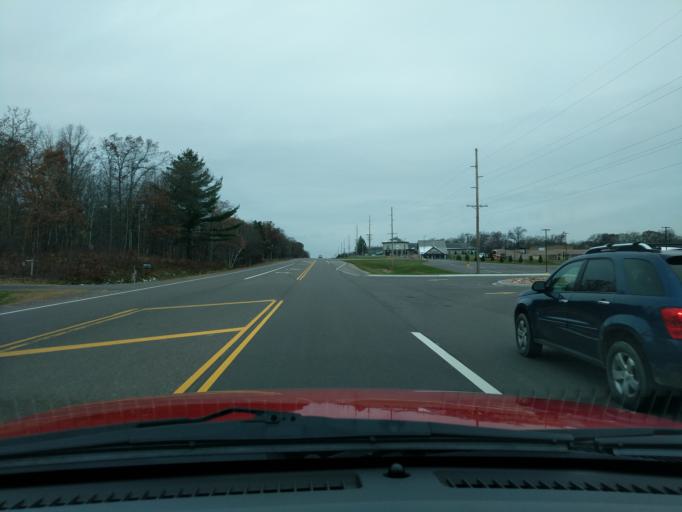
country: US
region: Wisconsin
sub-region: Burnett County
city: Siren
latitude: 45.8088
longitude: -92.1998
